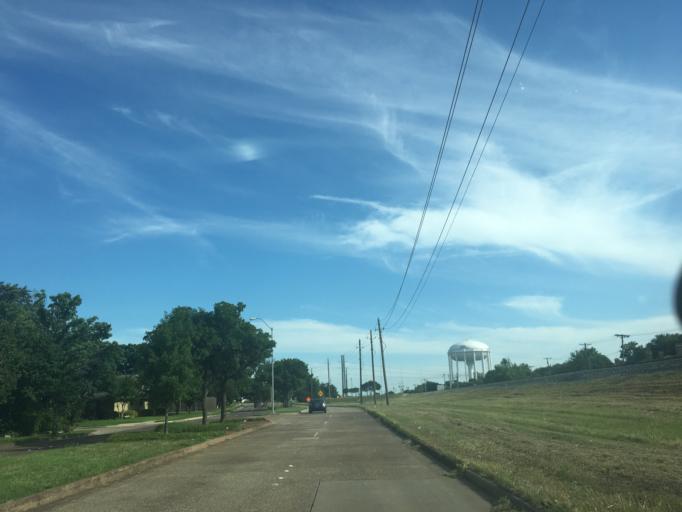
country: US
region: Texas
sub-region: Dallas County
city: Richardson
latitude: 32.9422
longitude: -96.7140
